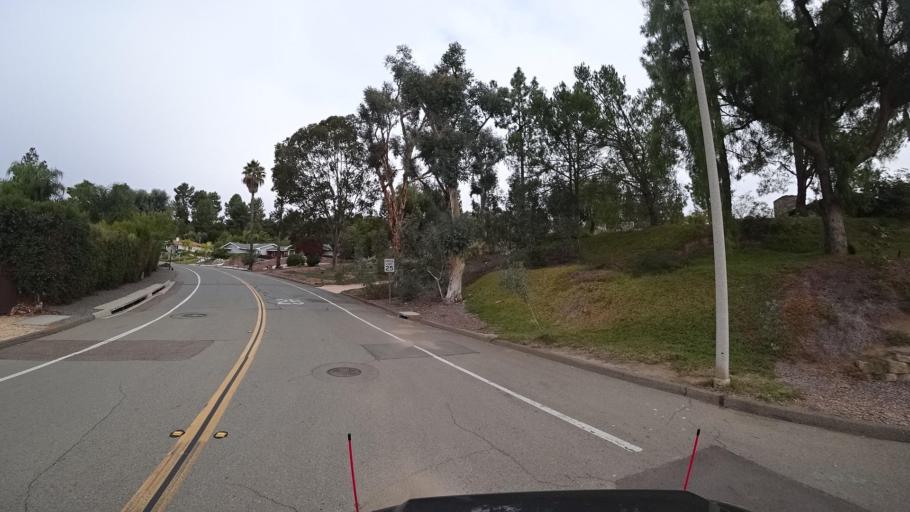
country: US
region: California
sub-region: San Diego County
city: Granite Hills
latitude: 32.7731
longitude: -116.9113
